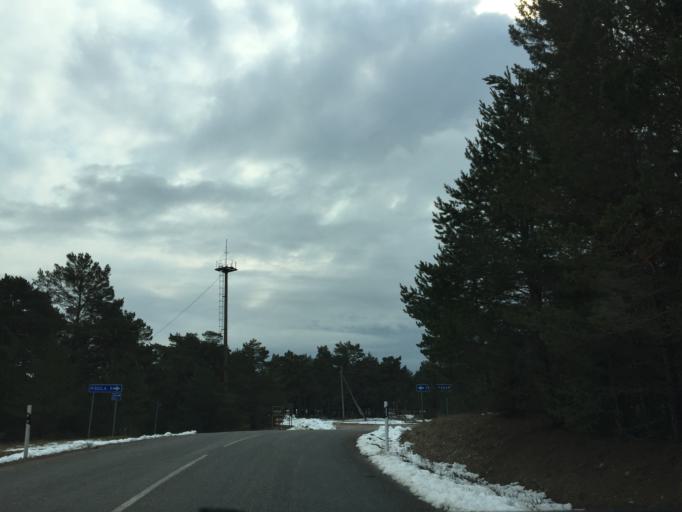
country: EE
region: Saare
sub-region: Kuressaare linn
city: Kuressaare
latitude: 58.4624
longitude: 22.0469
